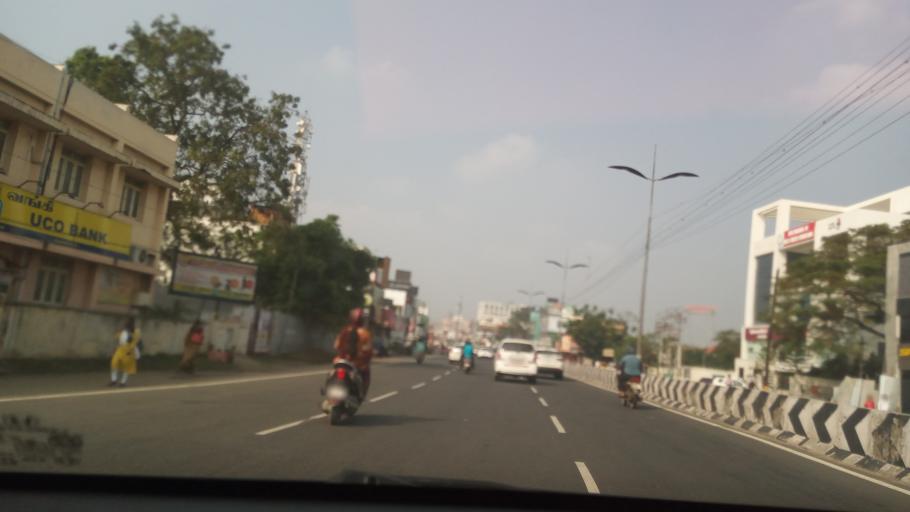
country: IN
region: Tamil Nadu
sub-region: Coimbatore
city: Coimbatore
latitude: 11.0221
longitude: 76.9976
